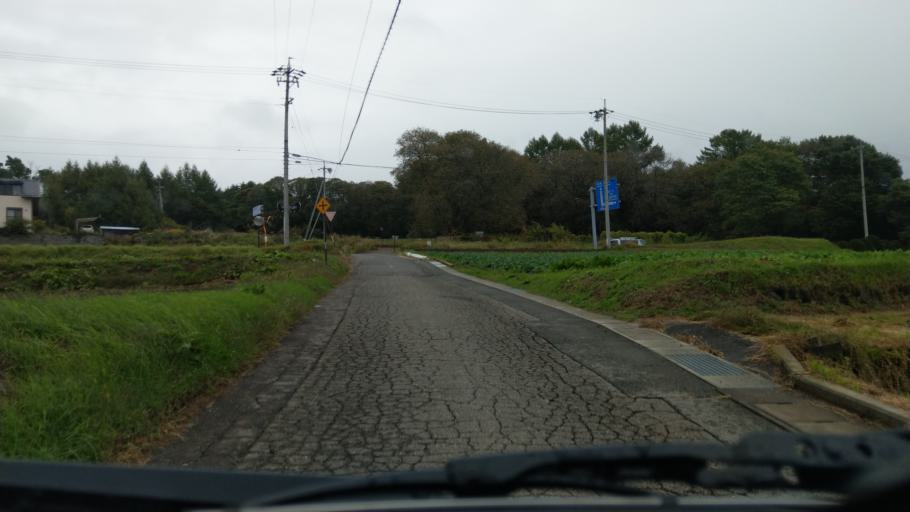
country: JP
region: Nagano
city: Komoro
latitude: 36.3390
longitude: 138.4559
